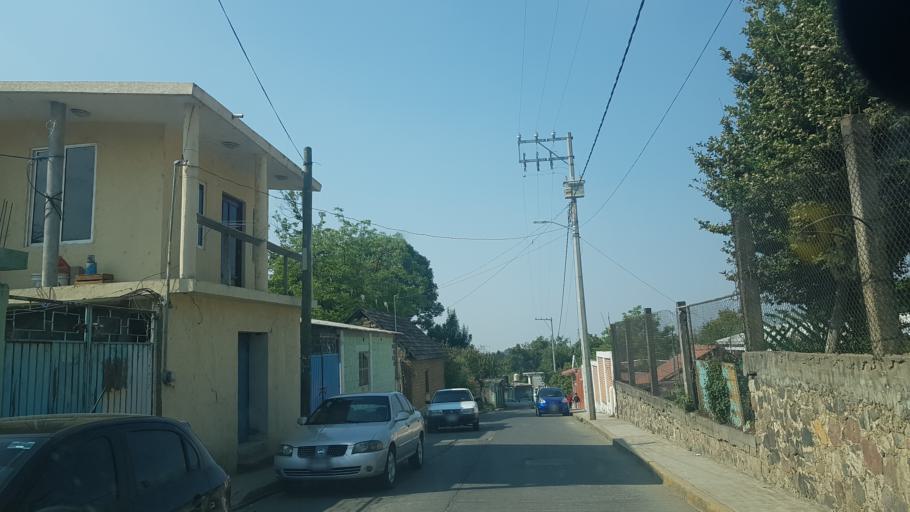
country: MX
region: Morelos
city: Hueyapan
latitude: 18.8845
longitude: -98.6893
